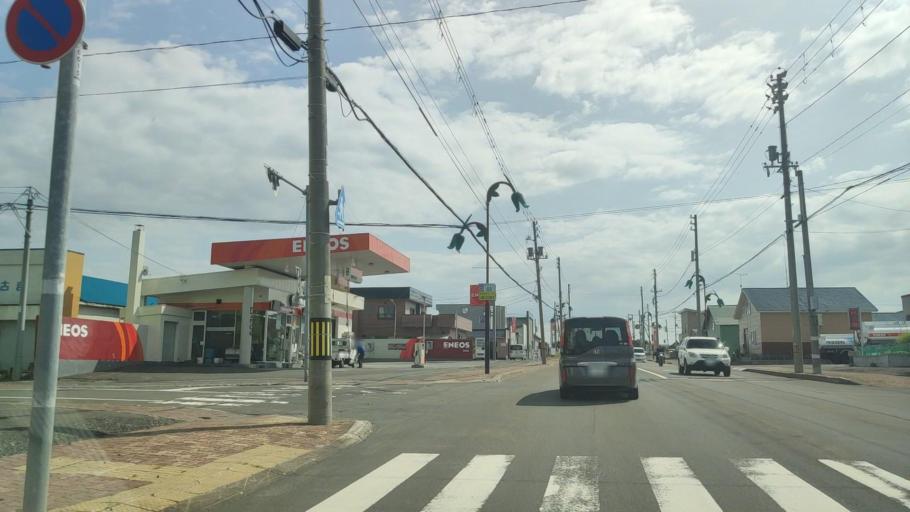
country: JP
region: Hokkaido
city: Rumoi
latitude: 44.3088
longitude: 141.6541
